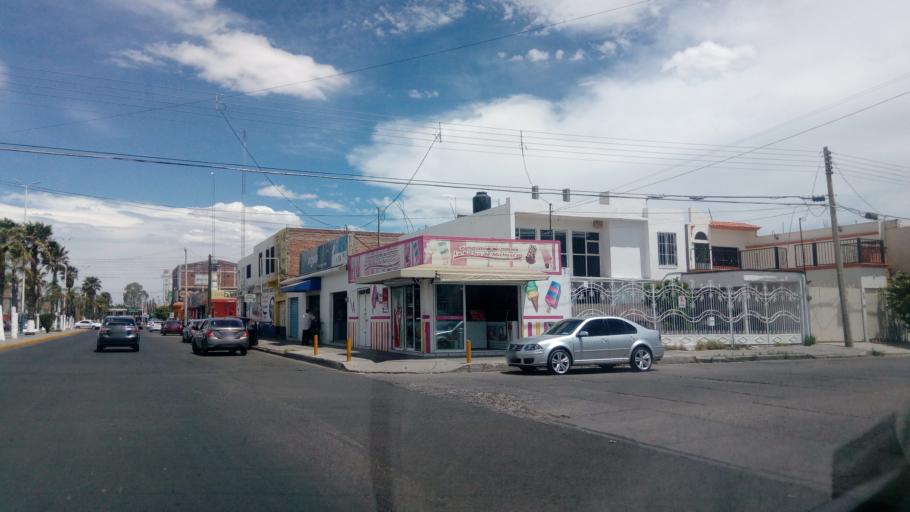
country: MX
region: Durango
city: Victoria de Durango
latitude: 23.9961
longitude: -104.6662
